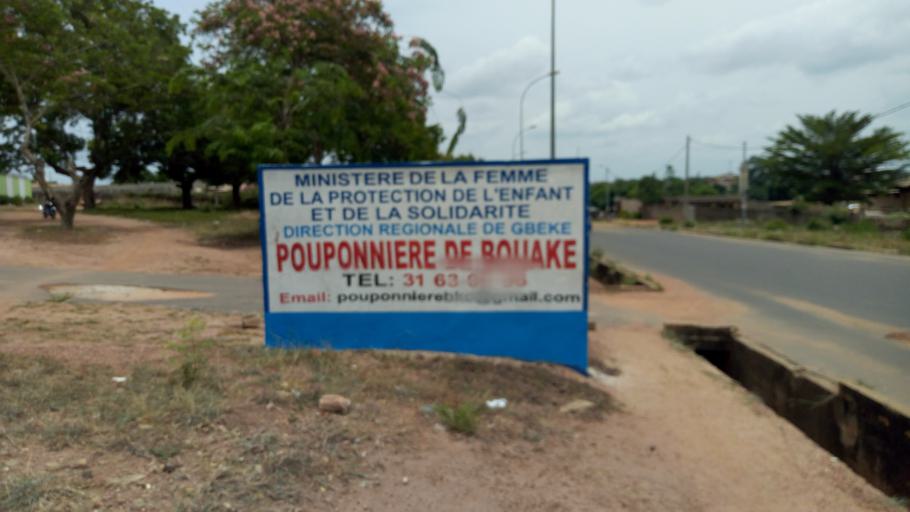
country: CI
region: Vallee du Bandama
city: Bouake
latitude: 7.7079
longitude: -5.0340
